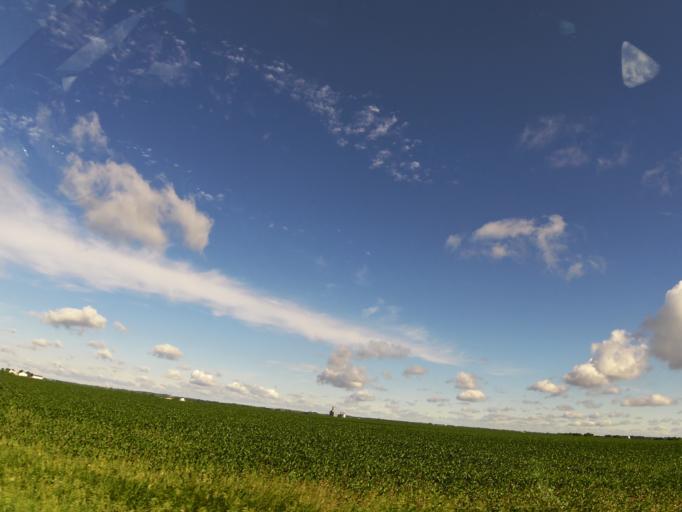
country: US
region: Minnesota
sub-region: Dakota County
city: Hastings
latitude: 44.6659
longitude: -92.9349
